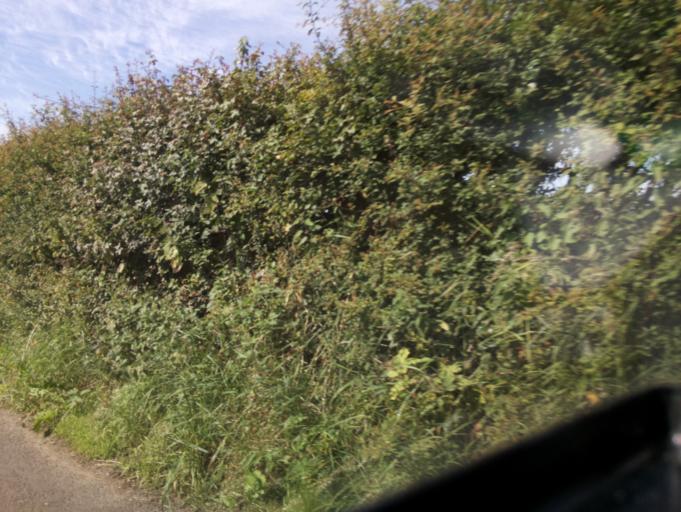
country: GB
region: England
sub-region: Wiltshire
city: Nettleton
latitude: 51.4833
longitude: -2.2668
